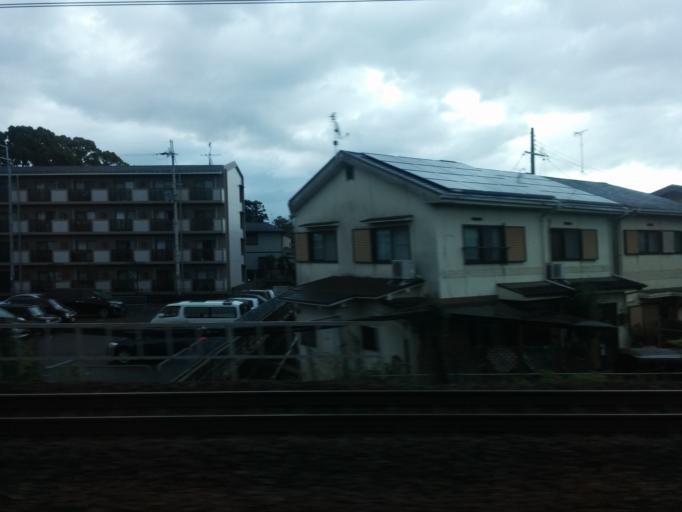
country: JP
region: Shiga Prefecture
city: Kusatsu
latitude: 35.0135
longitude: 135.9546
